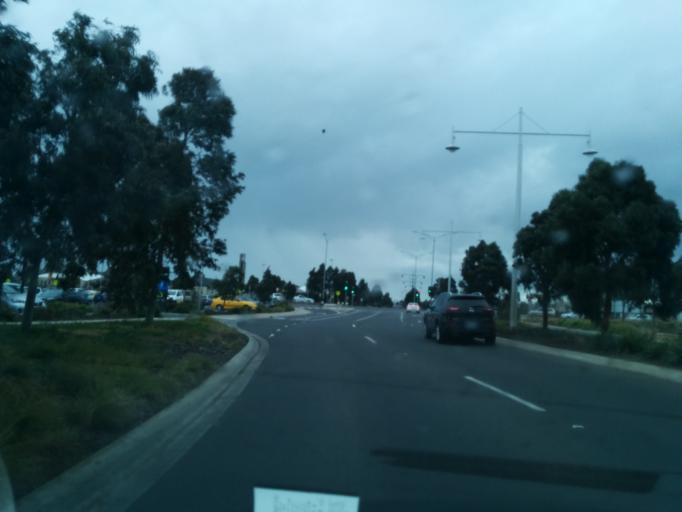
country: AU
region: Victoria
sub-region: Wyndham
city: Point Cook
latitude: -37.8983
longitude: 144.7279
